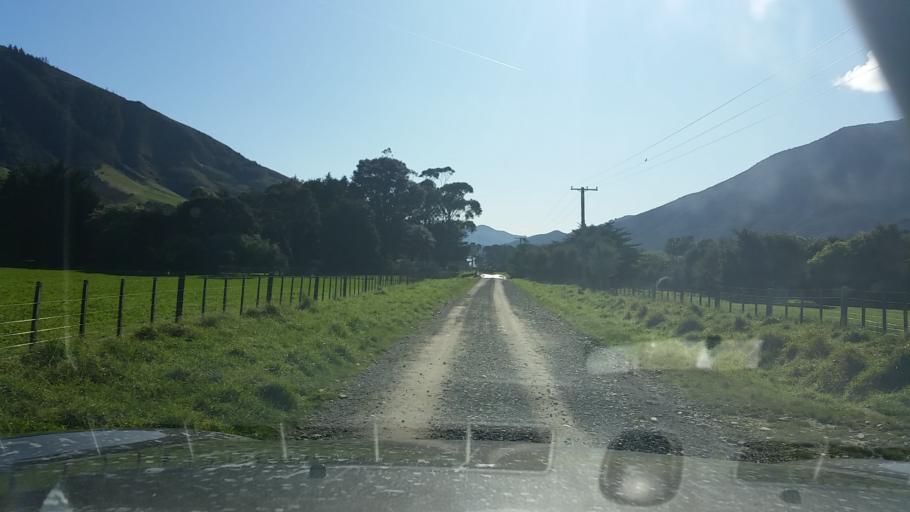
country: NZ
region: Marlborough
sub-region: Marlborough District
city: Picton
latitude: -41.1229
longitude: 174.0386
